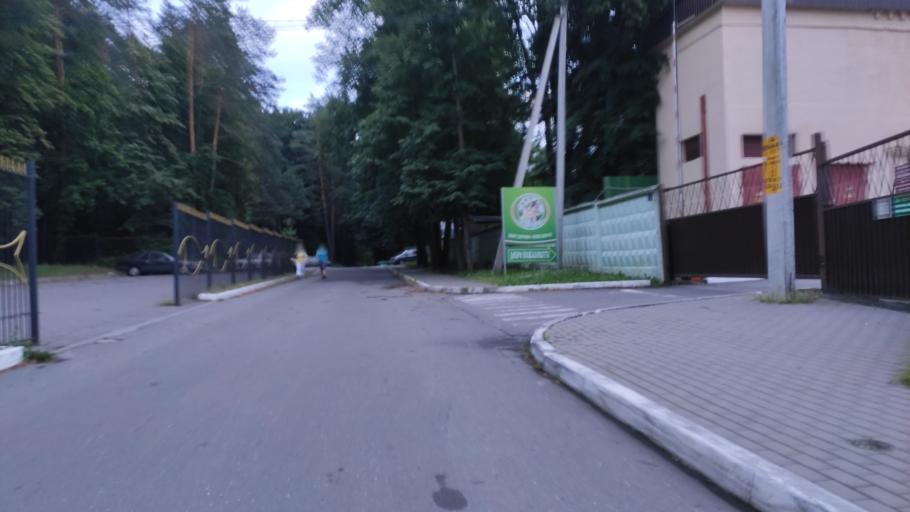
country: BY
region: Minsk
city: Zhdanovichy
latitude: 53.9680
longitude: 27.4317
